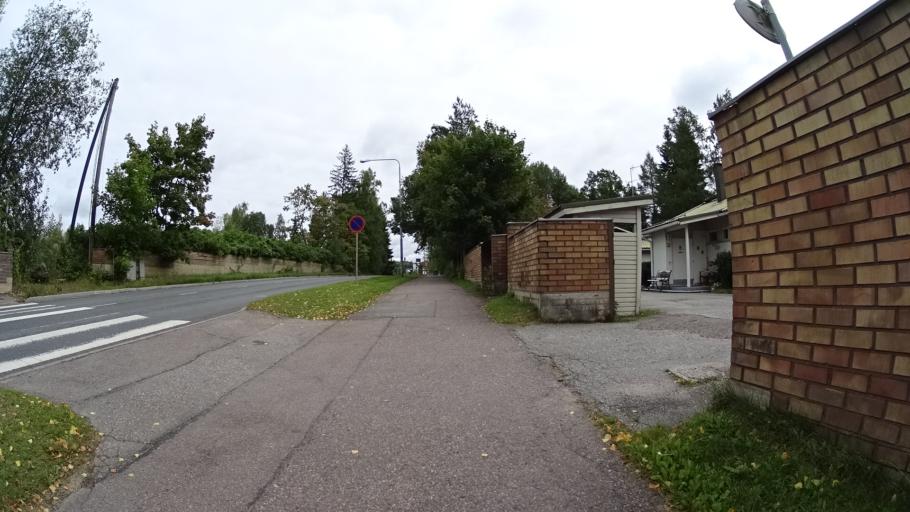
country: FI
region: Uusimaa
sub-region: Helsinki
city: Kilo
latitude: 60.2744
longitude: 24.8137
